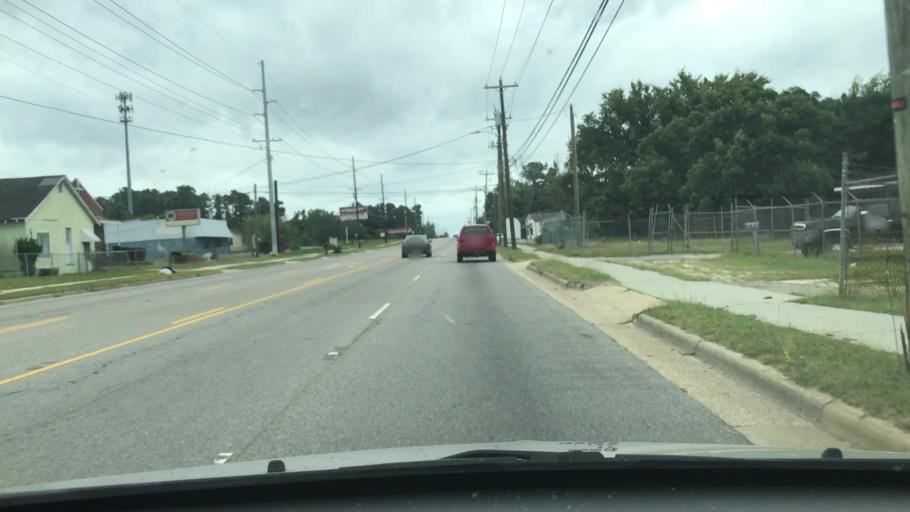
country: US
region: North Carolina
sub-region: Cumberland County
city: Fayetteville
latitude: 35.1065
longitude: -78.9236
